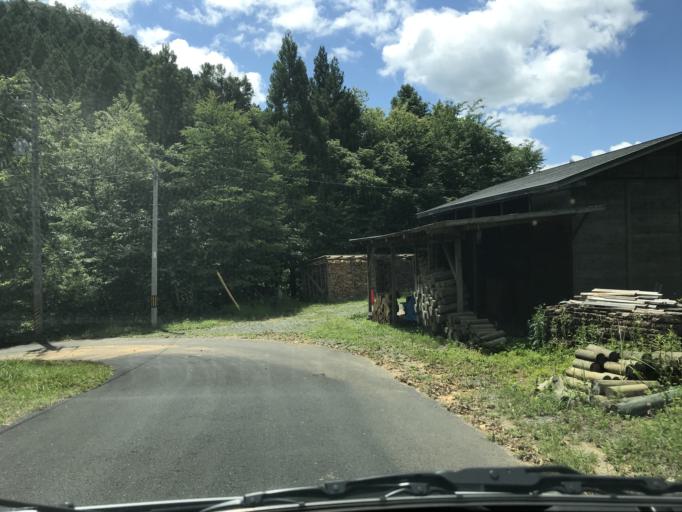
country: JP
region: Miyagi
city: Wakuya
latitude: 38.6856
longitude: 141.3460
